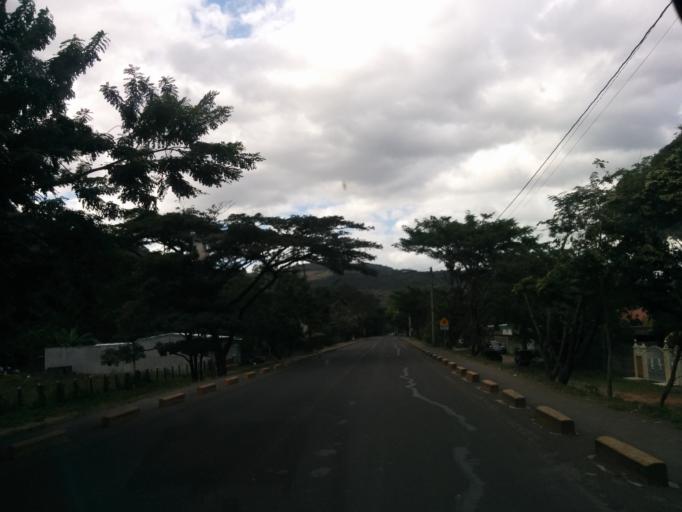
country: NI
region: Esteli
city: Esteli
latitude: 12.9588
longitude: -86.2278
